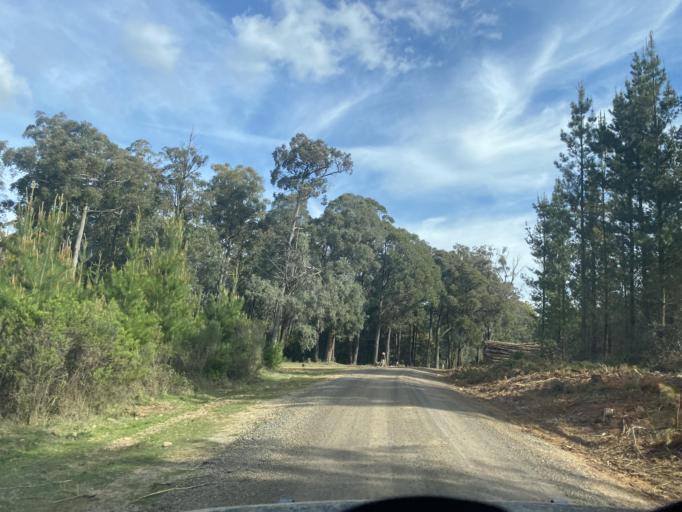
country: AU
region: Victoria
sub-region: Mansfield
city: Mansfield
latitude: -36.8413
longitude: 146.1830
